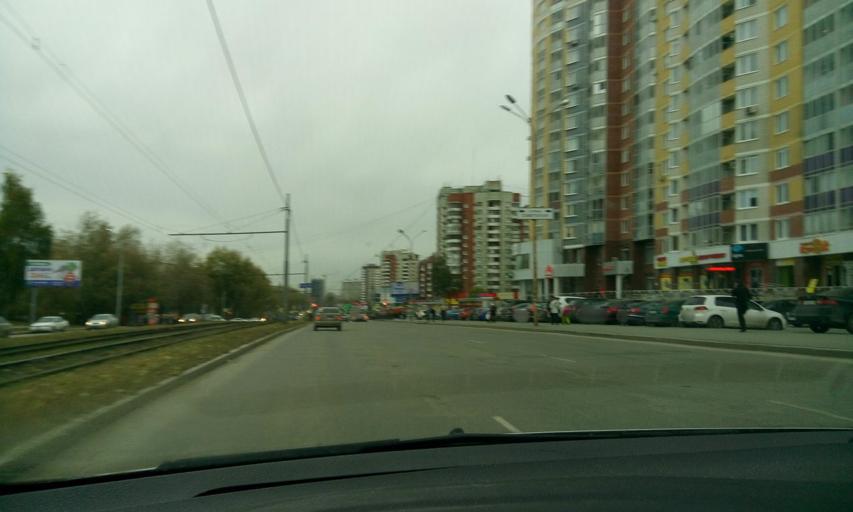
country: RU
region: Sverdlovsk
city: Yekaterinburg
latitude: 56.8531
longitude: 60.6383
